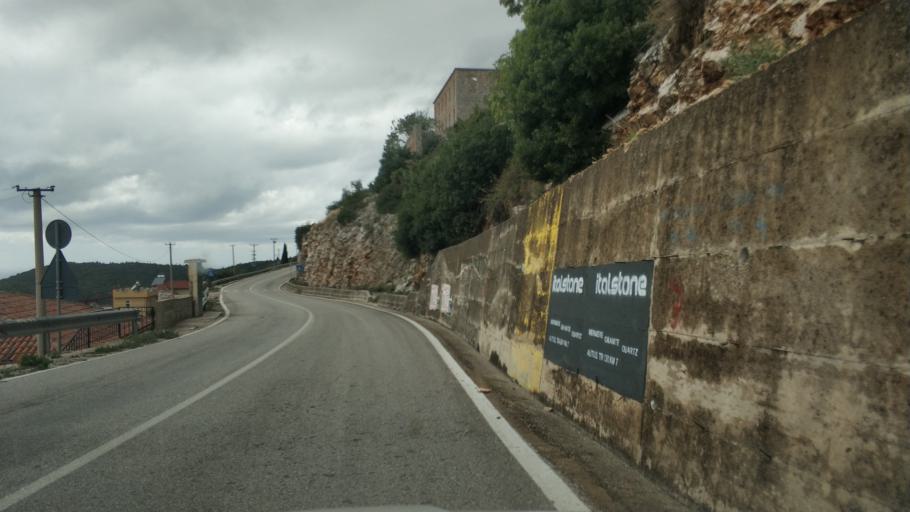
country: AL
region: Vlore
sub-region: Rrethi i Vlores
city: Himare
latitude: 40.1404
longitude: 19.6910
